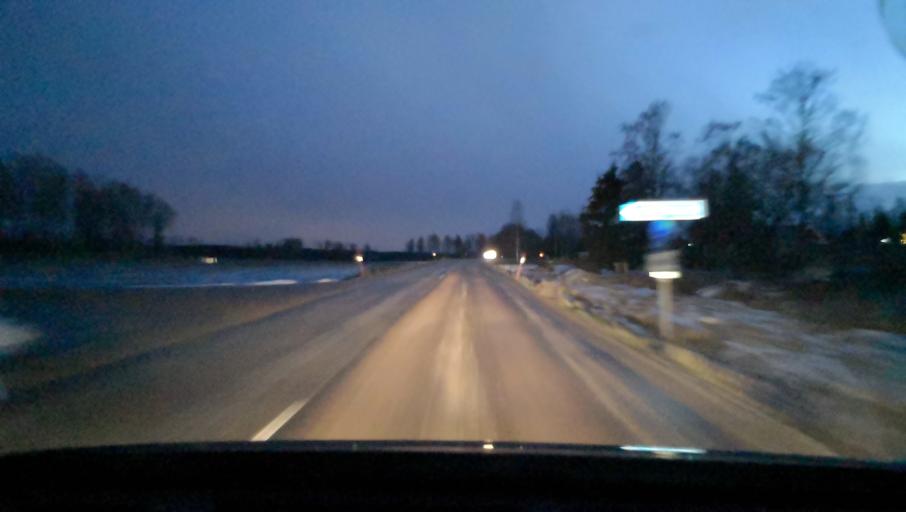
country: SE
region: Vaestmanland
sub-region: Vasteras
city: Skultuna
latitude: 59.7662
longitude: 16.4617
